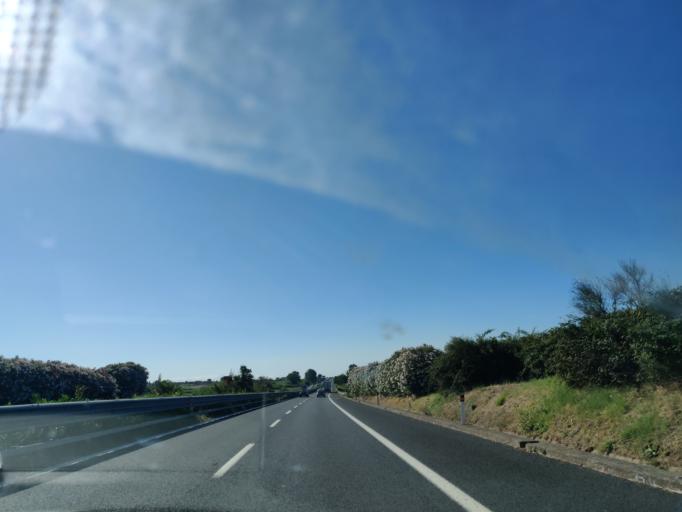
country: IT
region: Latium
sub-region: Citta metropolitana di Roma Capitale
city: Marina di Cerveteri
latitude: 41.9989
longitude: 12.0465
